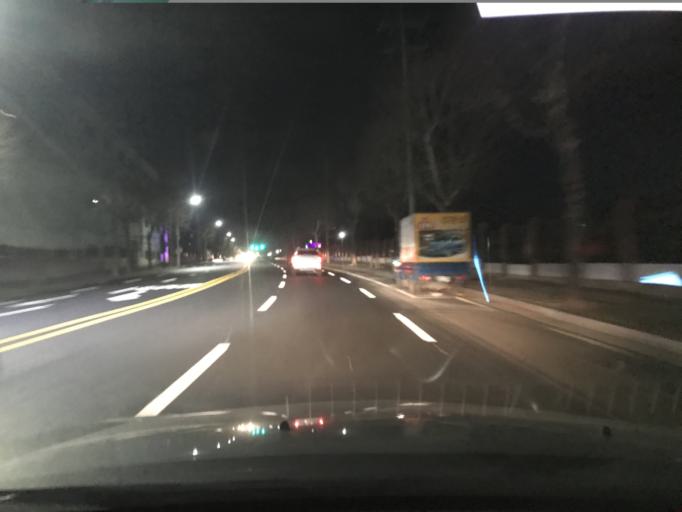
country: KR
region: Daegu
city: Hwawon
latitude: 35.7295
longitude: 128.4612
